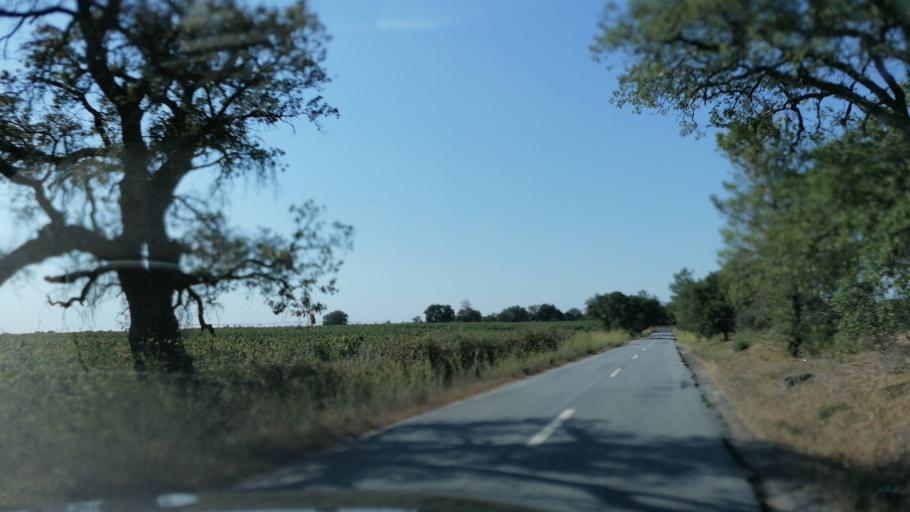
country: PT
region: Santarem
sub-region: Benavente
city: Poceirao
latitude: 38.7454
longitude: -8.6300
